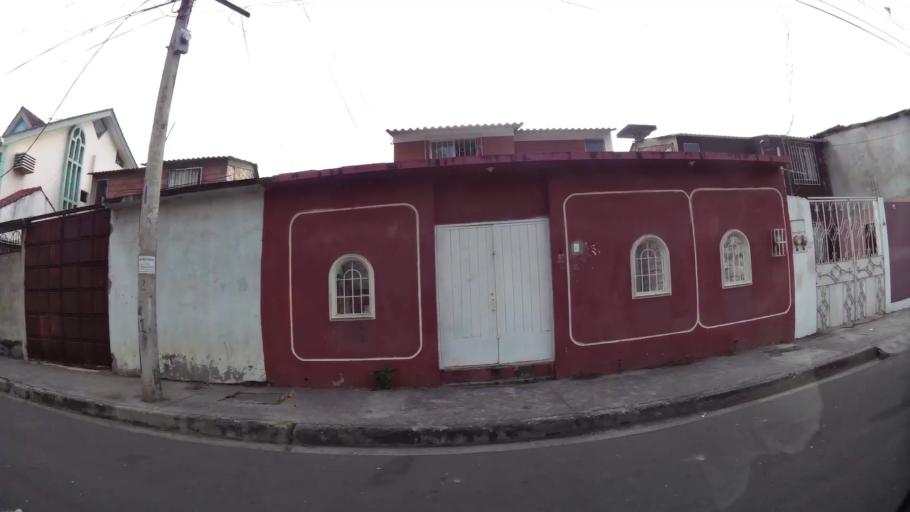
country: EC
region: Guayas
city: Eloy Alfaro
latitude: -2.1303
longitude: -79.8964
